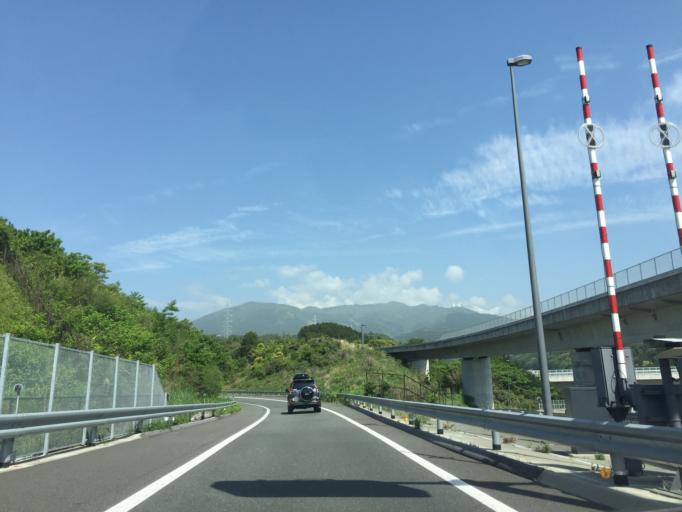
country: JP
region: Shizuoka
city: Numazu
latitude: 35.1550
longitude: 138.8686
